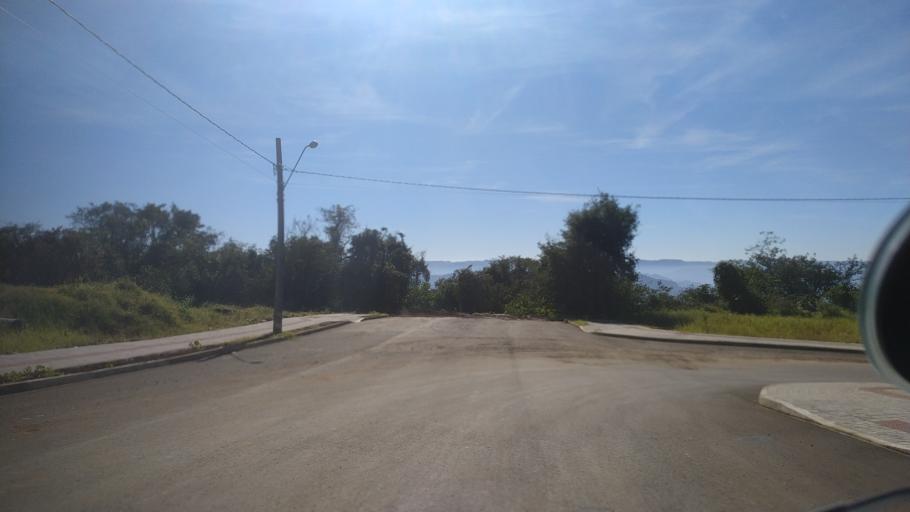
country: BR
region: Santa Catarina
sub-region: Chapeco
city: Chapeco
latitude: -27.0486
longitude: -52.6005
